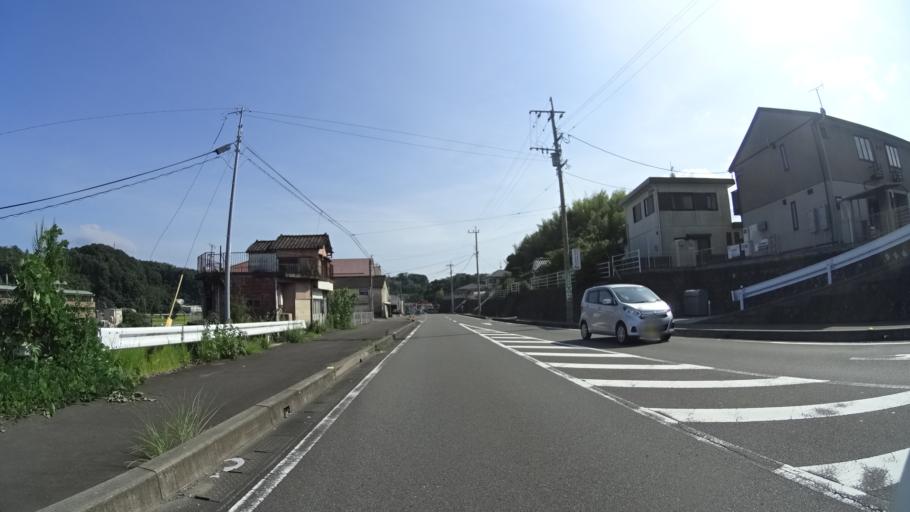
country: JP
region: Kagoshima
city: Kagoshima-shi
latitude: 31.6519
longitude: 130.5524
